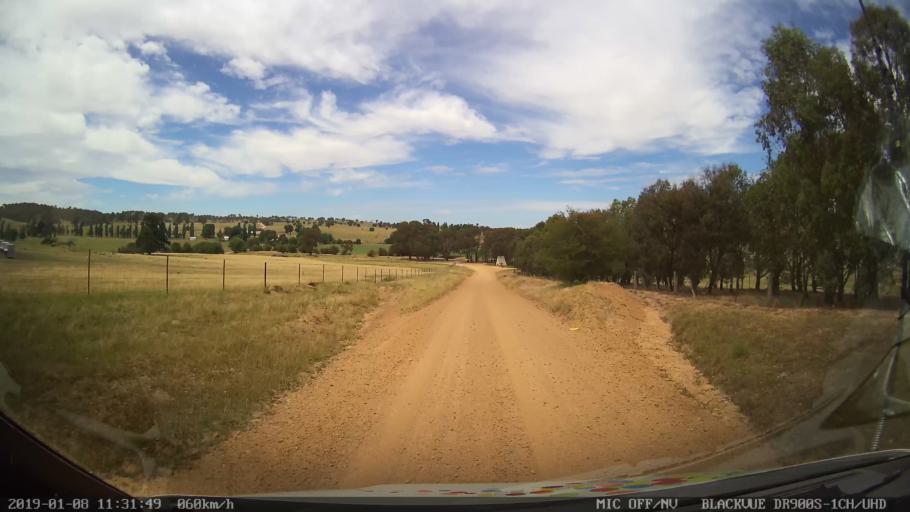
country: AU
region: New South Wales
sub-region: Guyra
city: Guyra
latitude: -30.3146
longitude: 151.5345
